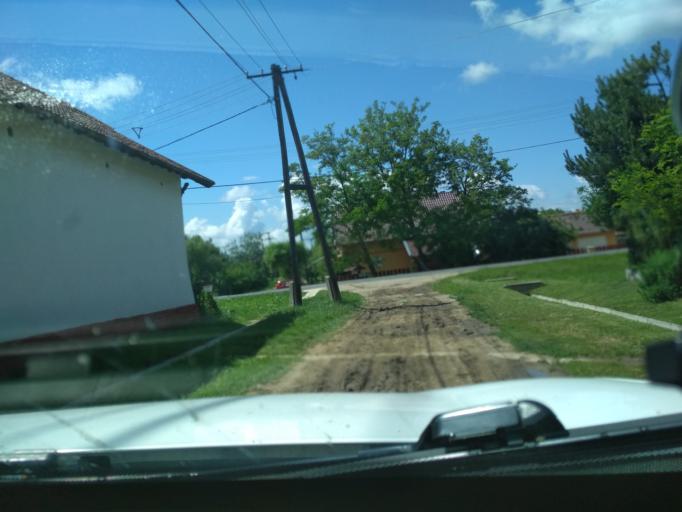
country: HU
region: Jasz-Nagykun-Szolnok
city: Abadszalok
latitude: 47.4827
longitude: 20.6072
